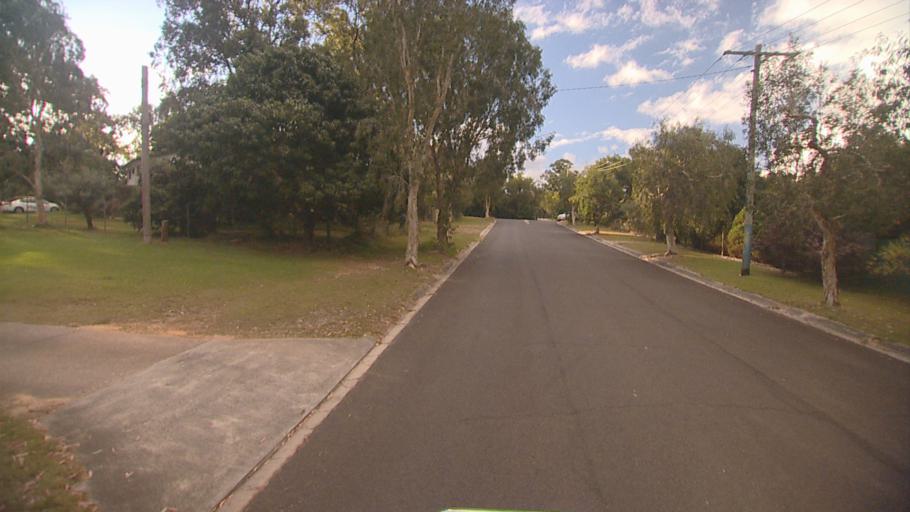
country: AU
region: Queensland
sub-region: Logan
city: Park Ridge South
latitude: -27.7012
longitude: 153.0204
